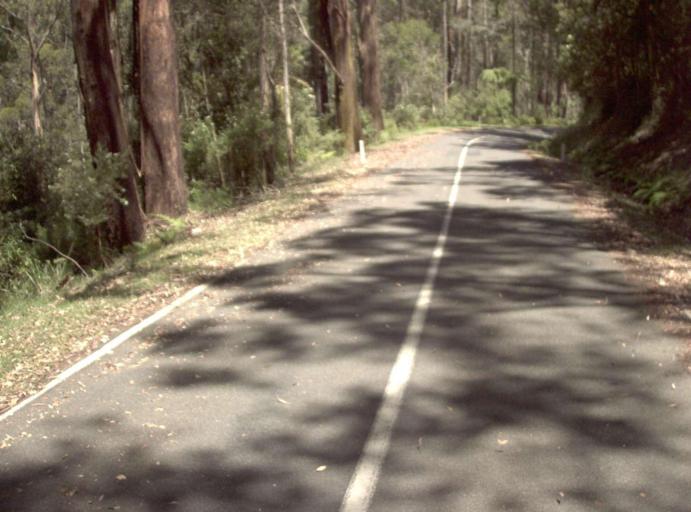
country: AU
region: Victoria
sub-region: Yarra Ranges
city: Millgrove
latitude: -37.7373
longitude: 145.7214
